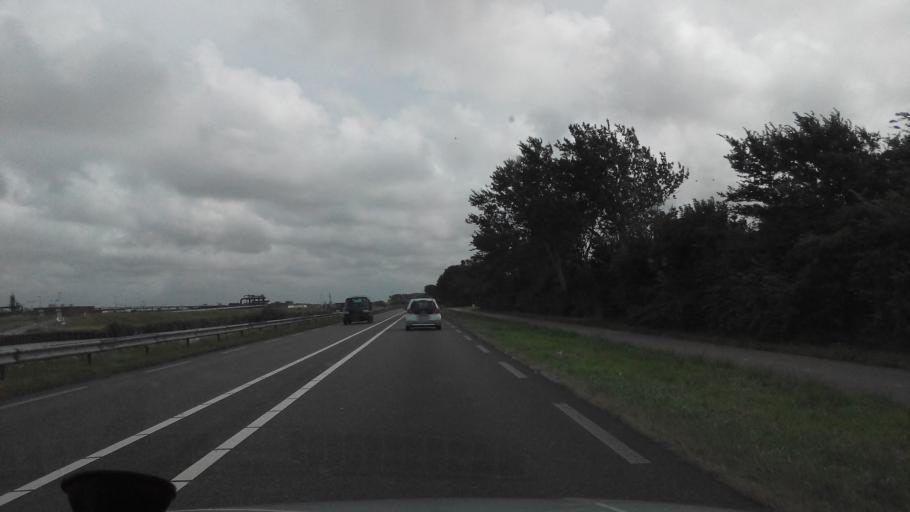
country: NL
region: North Holland
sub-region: Gemeente Den Helder
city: Den Helder
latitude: 52.9254
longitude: 4.7892
